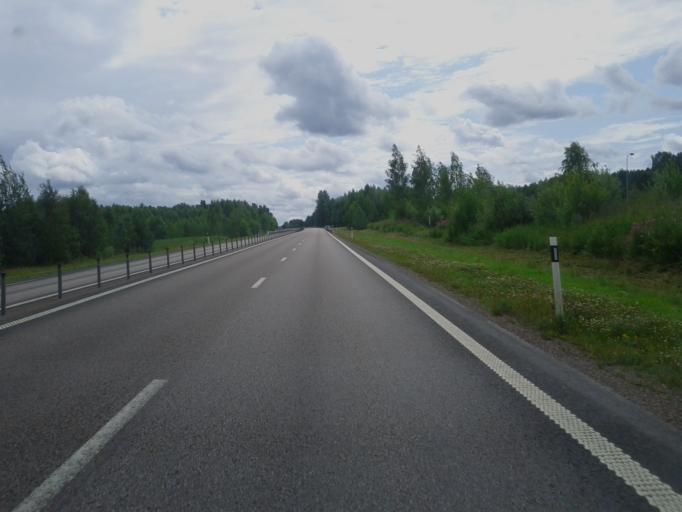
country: SE
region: Dalarna
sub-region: Borlange Kommun
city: Ornas
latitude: 60.4389
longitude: 15.5082
